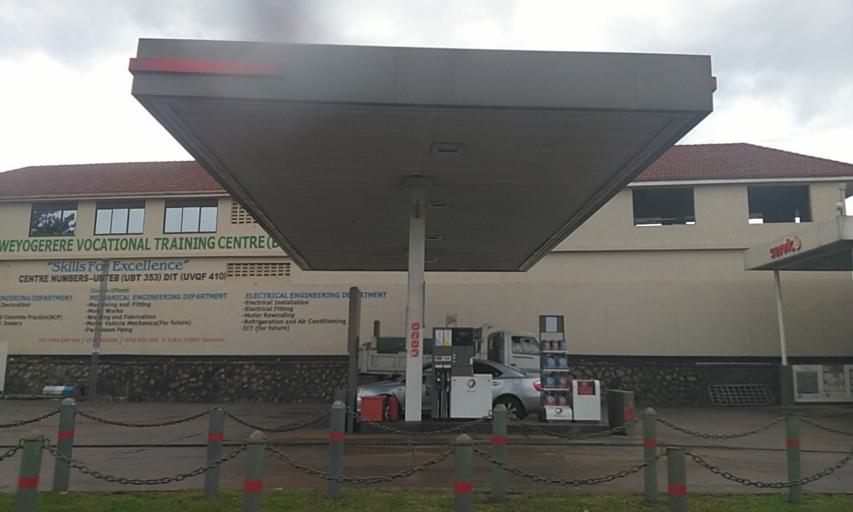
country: UG
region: Central Region
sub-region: Wakiso District
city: Bweyogerere
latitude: 0.3537
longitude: 32.6714
